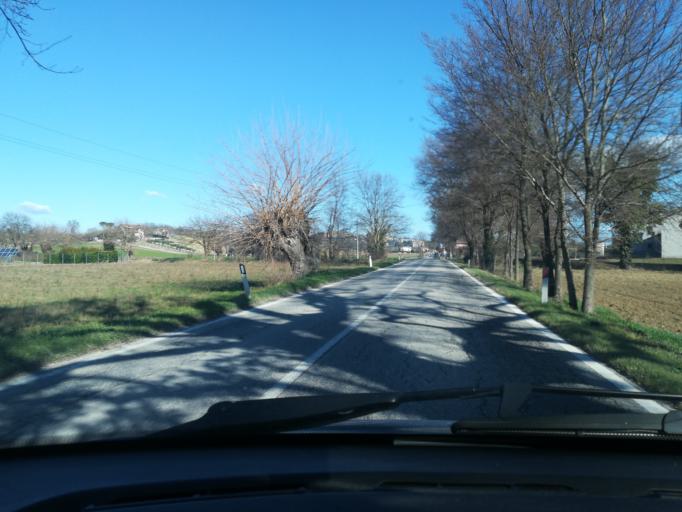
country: IT
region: The Marches
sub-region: Provincia di Macerata
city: Villa Potenza
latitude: 43.3361
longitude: 13.4281
